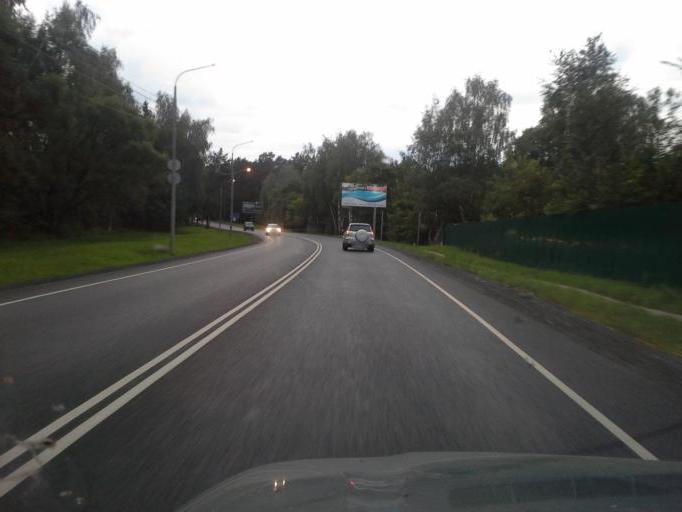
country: RU
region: Moskovskaya
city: Nikolina Gora
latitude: 55.7117
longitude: 37.0646
